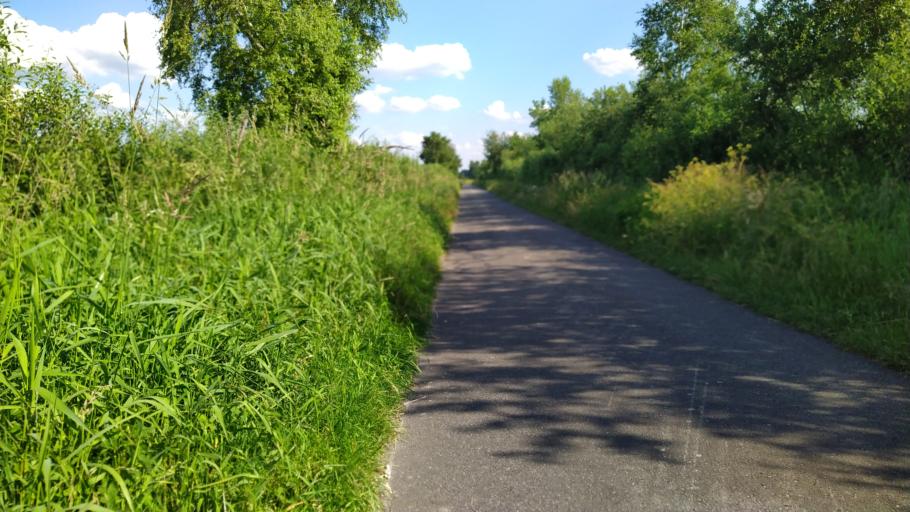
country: DE
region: Lower Saxony
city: Lintig
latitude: 53.6198
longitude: 8.8682
